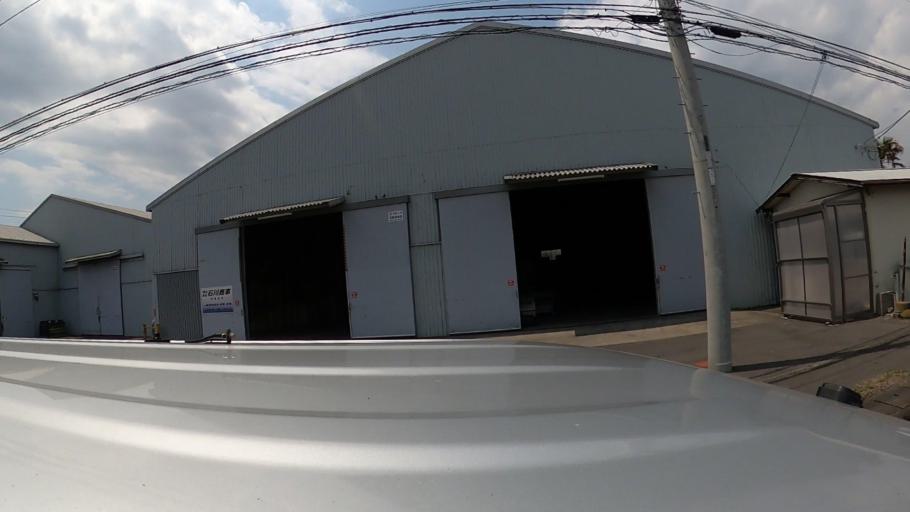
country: JP
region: Kanagawa
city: Chigasaki
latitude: 35.3871
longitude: 139.4021
